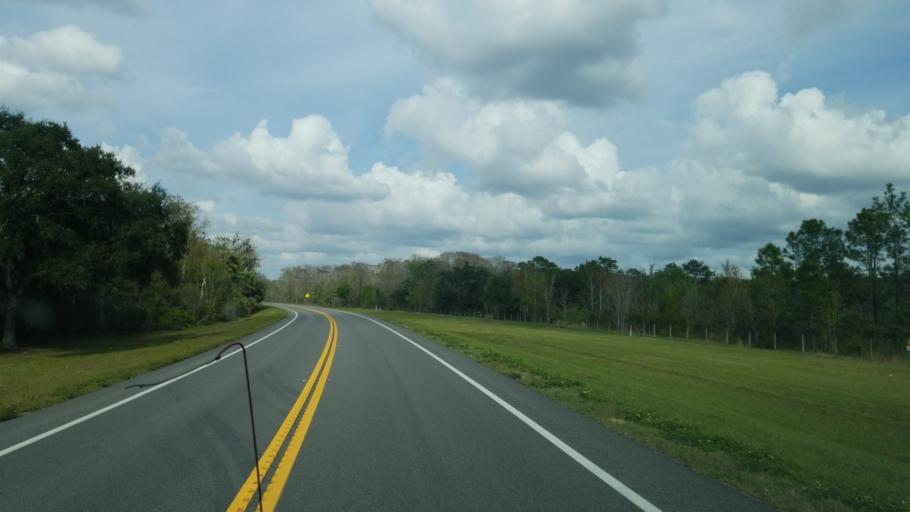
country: US
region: Florida
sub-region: Indian River County
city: Fellsmere
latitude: 27.7481
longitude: -80.9018
